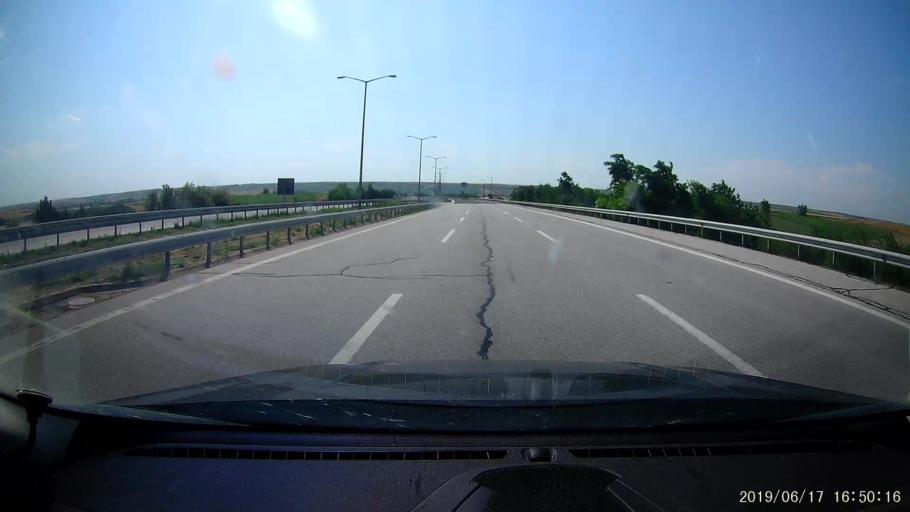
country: TR
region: Kirklareli
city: Babaeski
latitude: 41.5209
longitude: 27.0938
